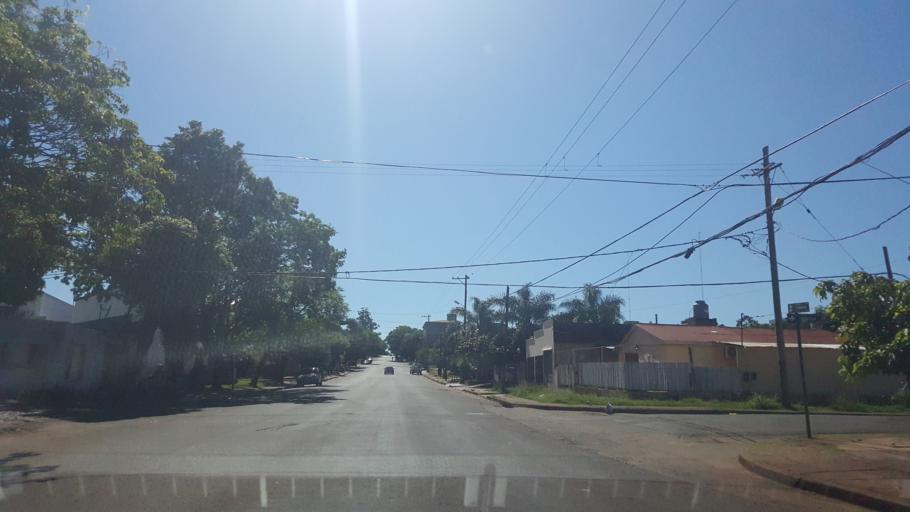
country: AR
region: Misiones
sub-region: Departamento de Capital
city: Posadas
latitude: -27.3903
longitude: -55.9064
